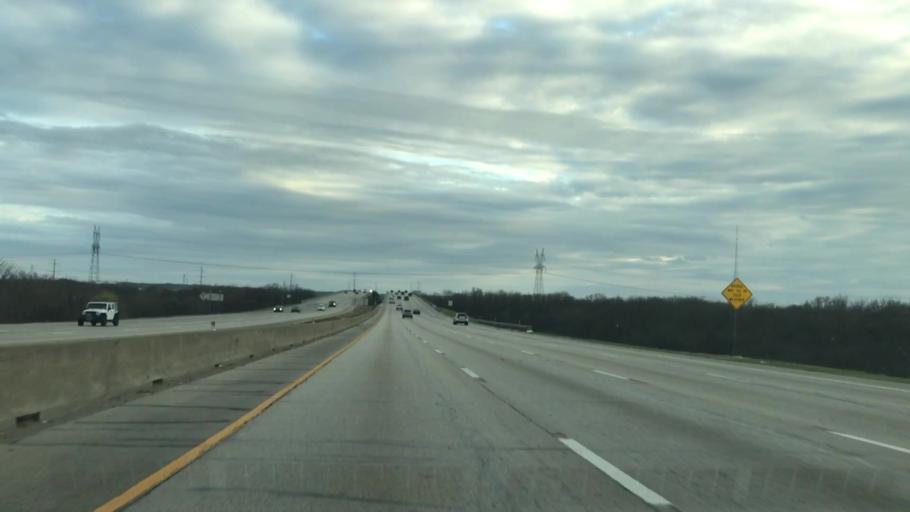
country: US
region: Texas
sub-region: Dallas County
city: Irving
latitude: 32.7922
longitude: -96.9203
